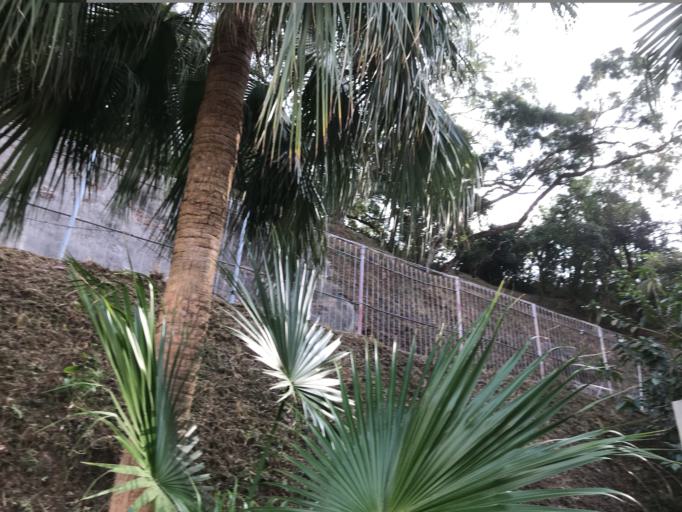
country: HK
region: Tai Po
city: Tai Po
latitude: 22.4623
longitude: 114.1612
